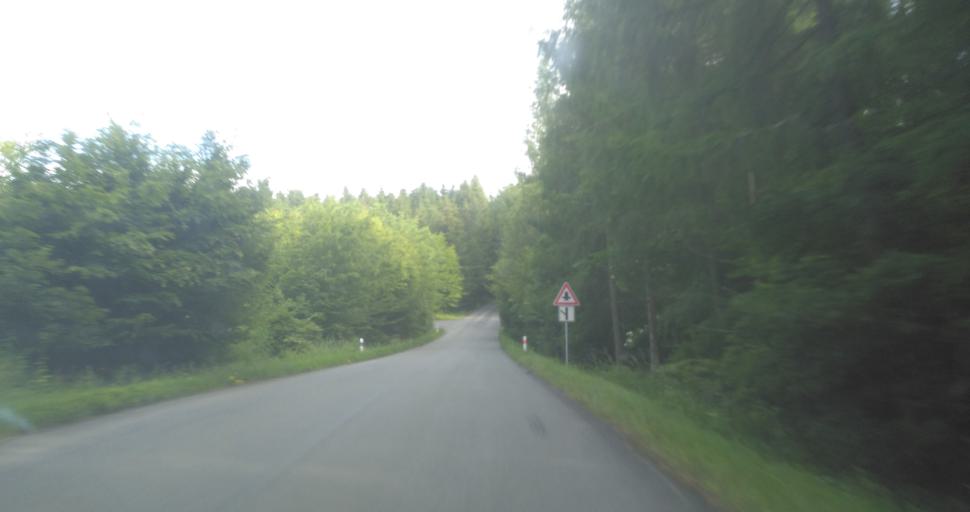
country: CZ
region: Central Bohemia
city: Hudlice
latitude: 49.9564
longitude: 13.9194
